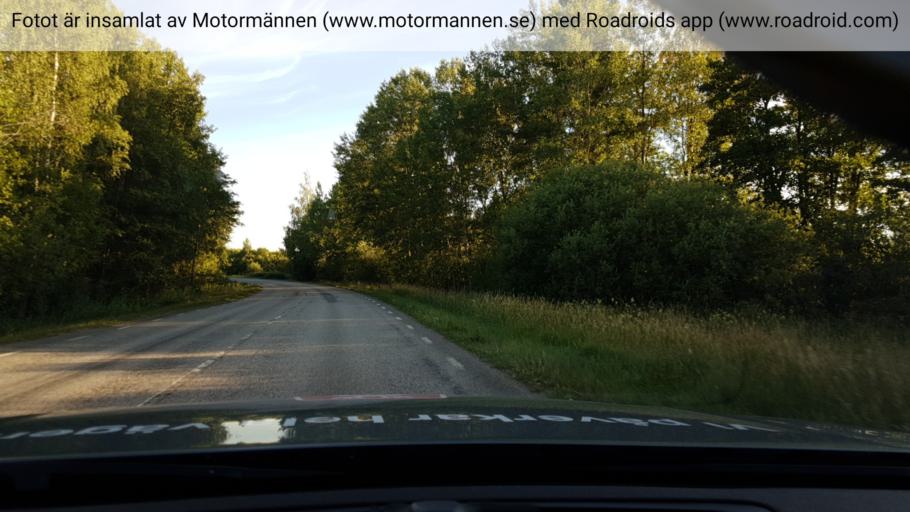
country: SE
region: Vaestmanland
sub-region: Vasteras
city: Skultuna
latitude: 59.7321
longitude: 16.4333
